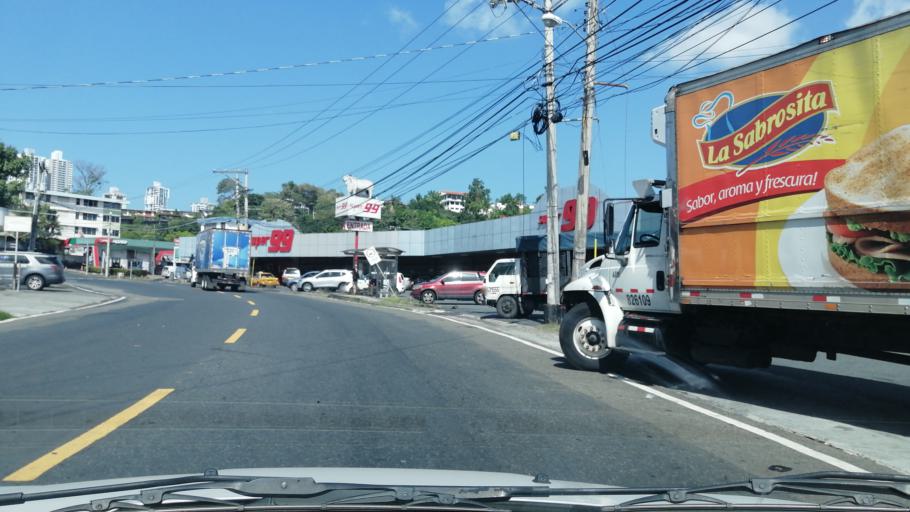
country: PA
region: Panama
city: Panama
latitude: 9.0111
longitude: -79.5247
